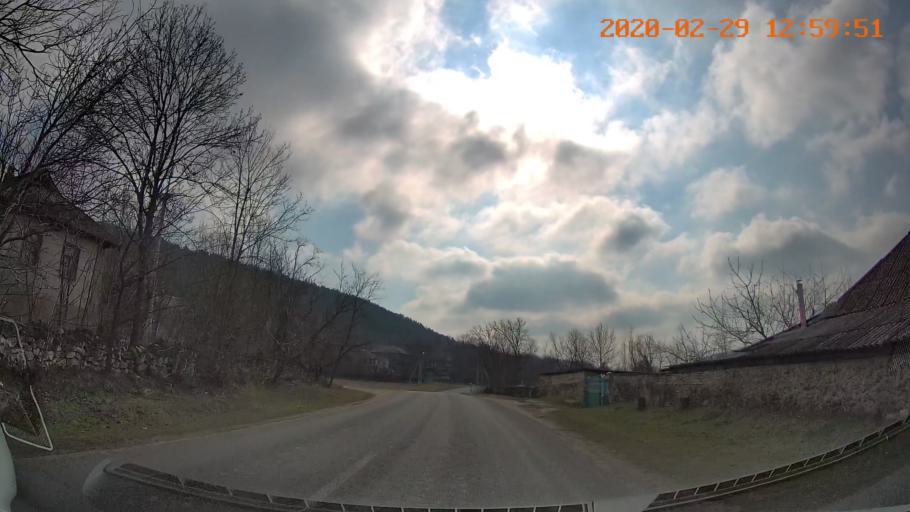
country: MD
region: Telenesti
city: Camenca
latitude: 48.0578
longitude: 28.7248
